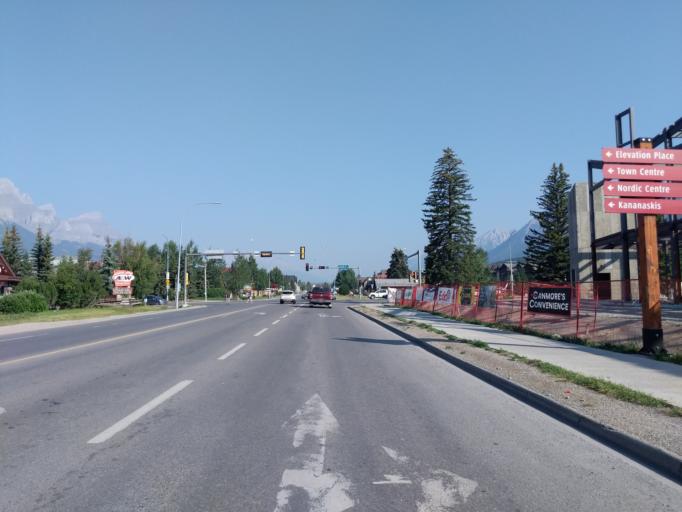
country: CA
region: Alberta
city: Canmore
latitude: 51.0876
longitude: -115.3470
